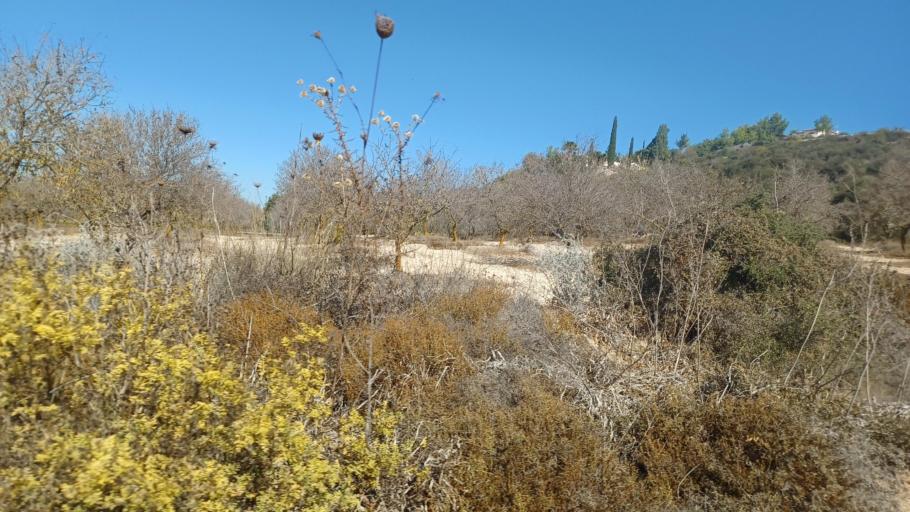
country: CY
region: Pafos
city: Mesogi
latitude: 34.8040
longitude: 32.4880
